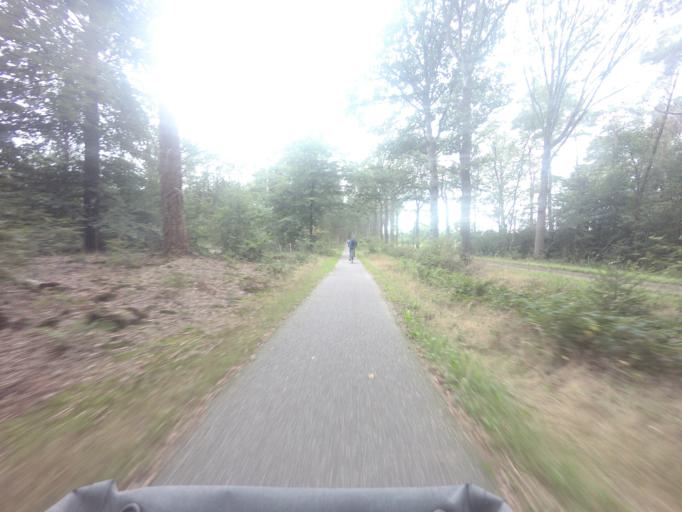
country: NL
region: Friesland
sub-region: Gemeente Weststellingwerf
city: Noordwolde
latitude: 52.9001
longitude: 6.2330
